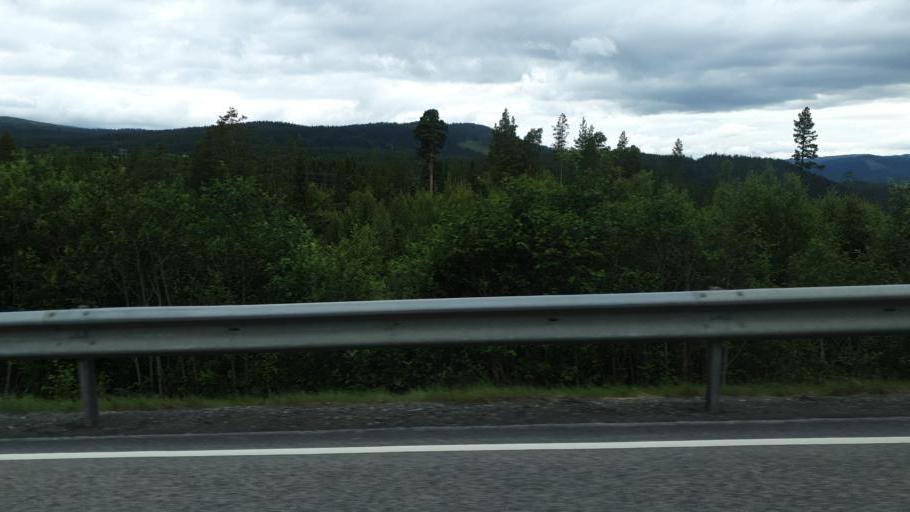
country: NO
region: Sor-Trondelag
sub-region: Rennebu
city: Berkak
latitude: 62.7972
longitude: 10.0226
